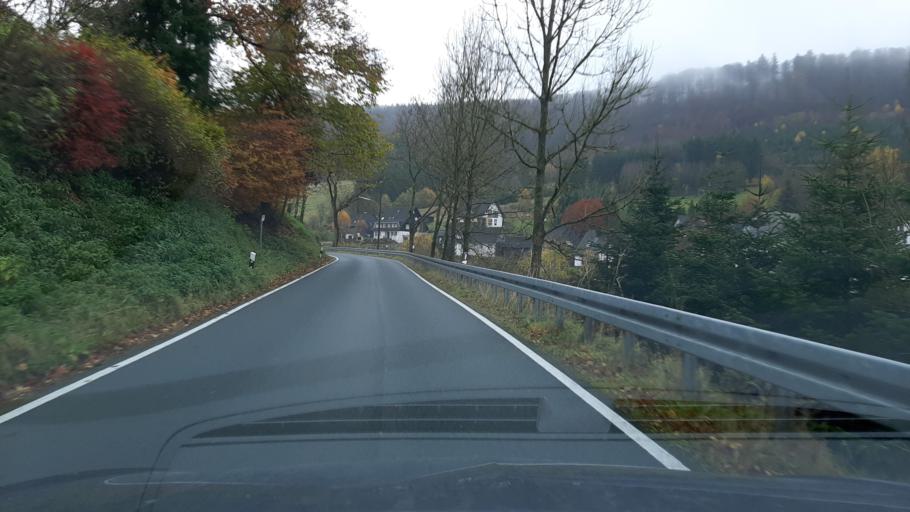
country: DE
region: North Rhine-Westphalia
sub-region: Regierungsbezirk Arnsberg
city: Bad Fredeburg
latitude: 51.1969
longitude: 8.4066
